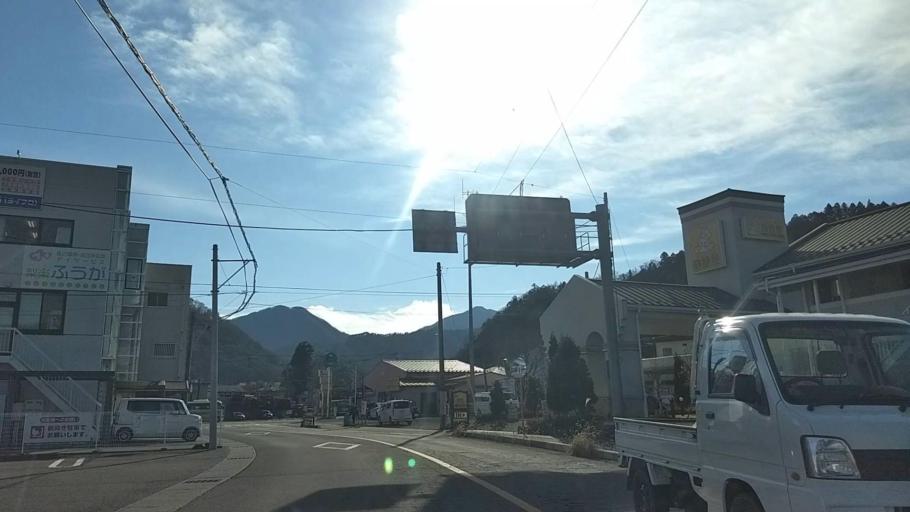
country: JP
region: Yamanashi
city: Otsuki
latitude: 35.5575
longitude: 138.9080
